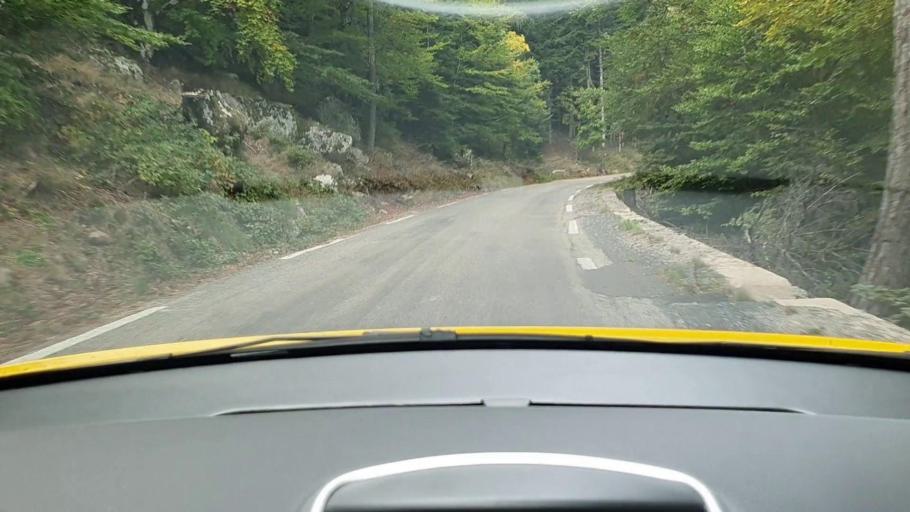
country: FR
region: Languedoc-Roussillon
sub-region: Departement du Gard
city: Le Vigan
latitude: 44.0314
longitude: 3.5724
